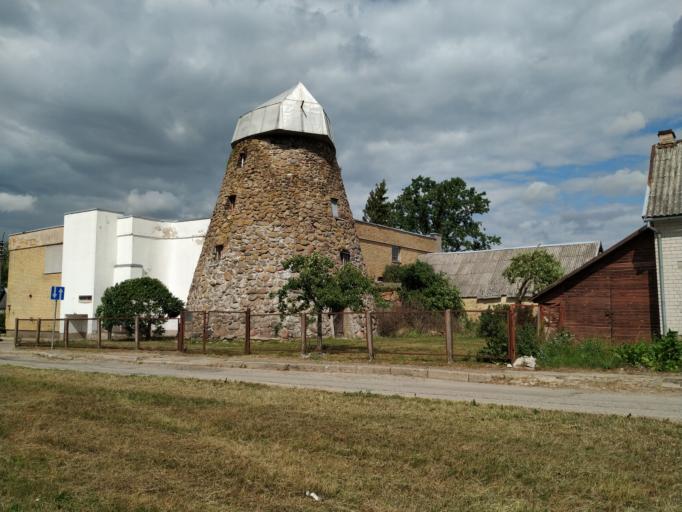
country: LT
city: Kupiskis
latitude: 55.8379
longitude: 24.9671
